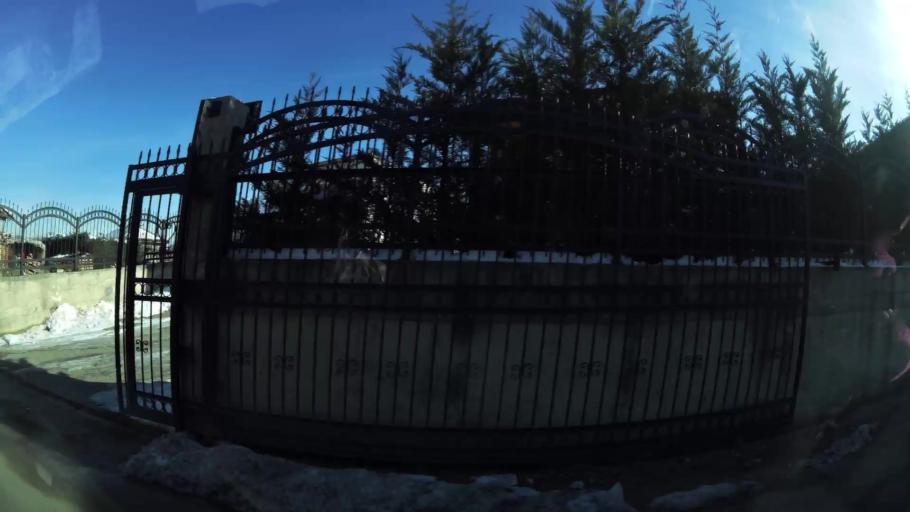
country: MK
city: Grchec
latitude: 41.9758
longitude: 21.3094
